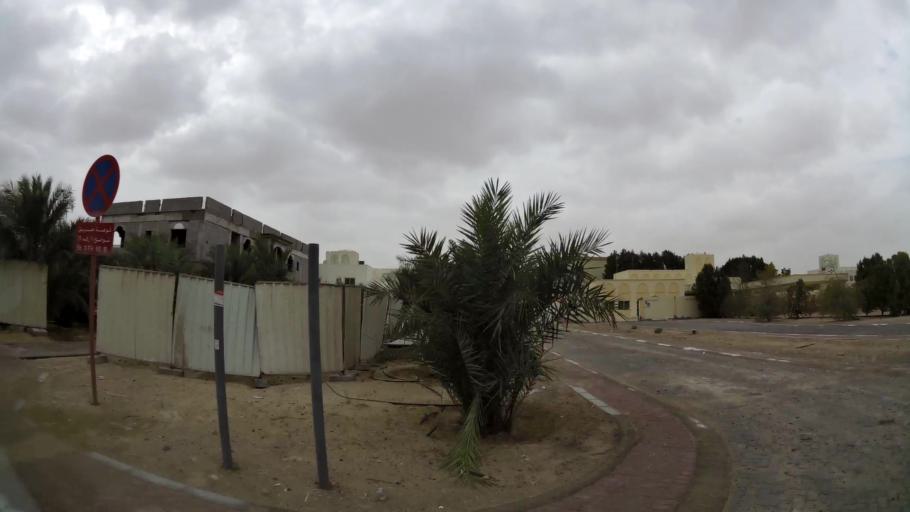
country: AE
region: Abu Dhabi
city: Abu Dhabi
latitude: 24.3305
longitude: 54.6448
